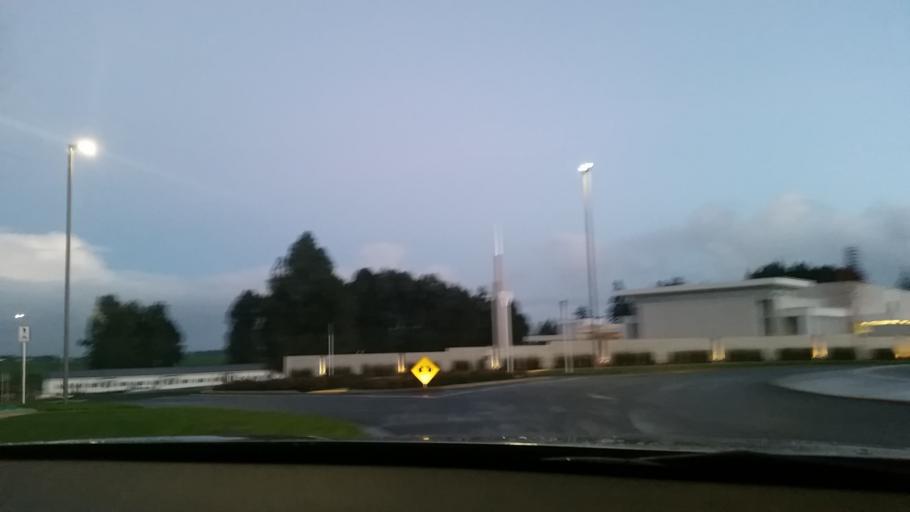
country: NZ
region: Waikato
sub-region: Hamilton City
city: Hamilton
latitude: -37.8220
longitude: 175.2262
